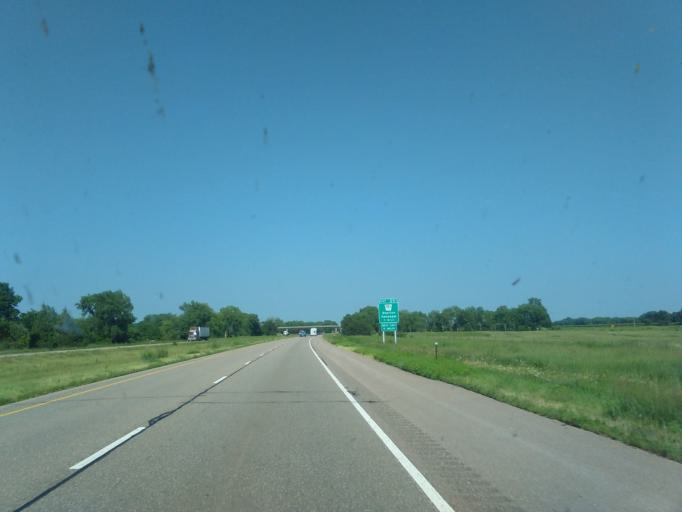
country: US
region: Nebraska
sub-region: Buffalo County
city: Shelton
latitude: 40.7214
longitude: -98.7663
